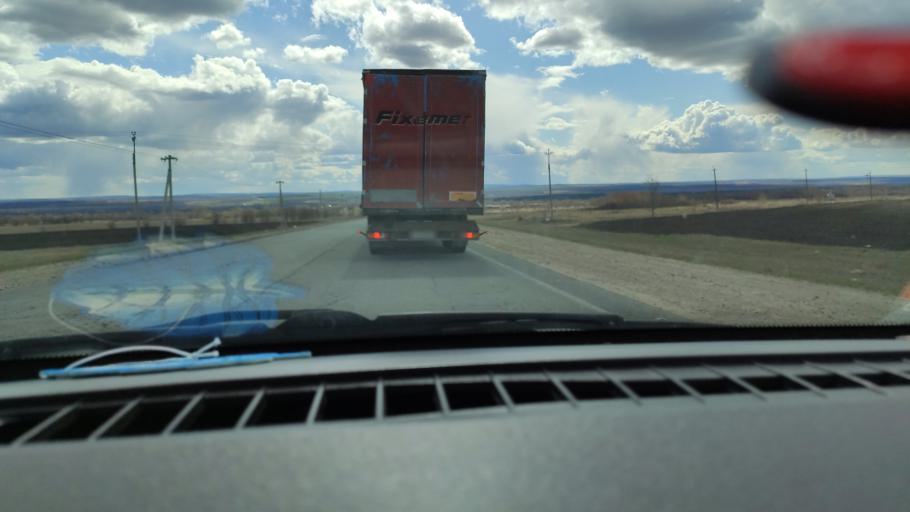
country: RU
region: Samara
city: Varlamovo
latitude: 53.1790
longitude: 48.2849
